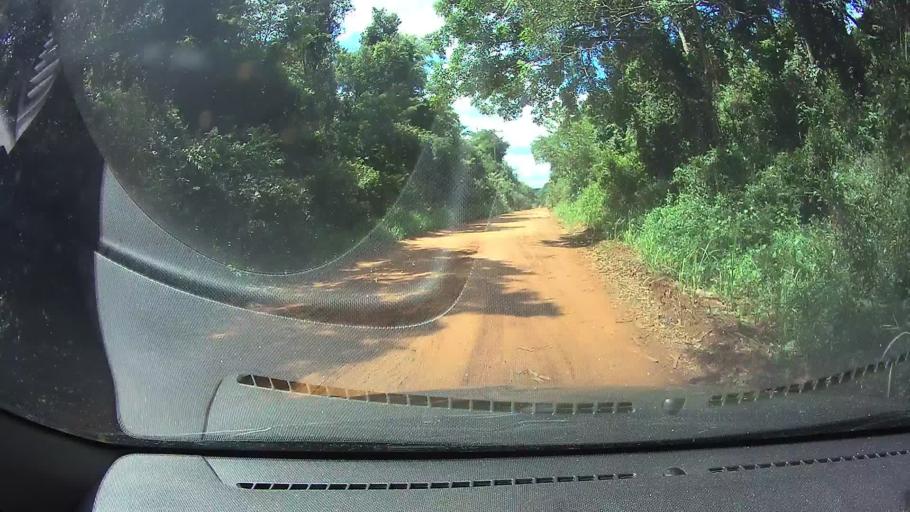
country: PY
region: Paraguari
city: La Colmena
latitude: -25.9459
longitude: -56.7806
